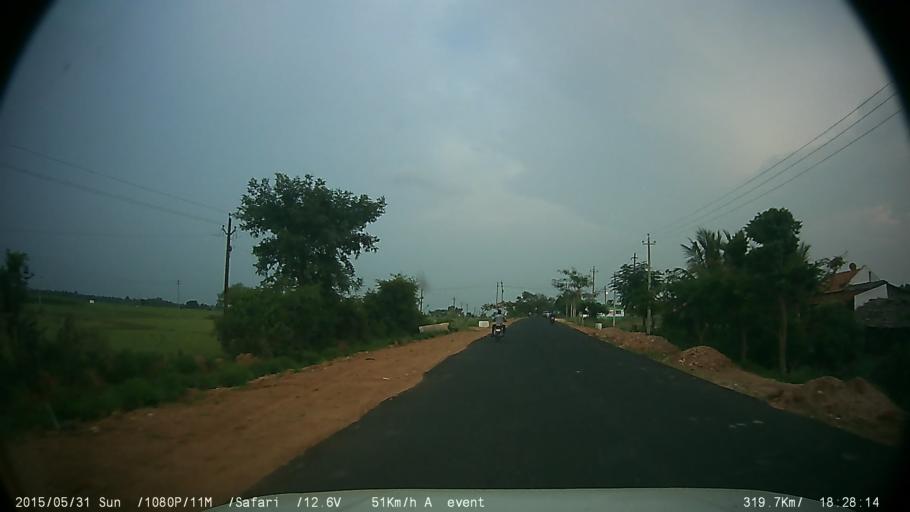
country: IN
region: Karnataka
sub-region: Mysore
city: Nanjangud
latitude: 12.1221
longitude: 76.7206
